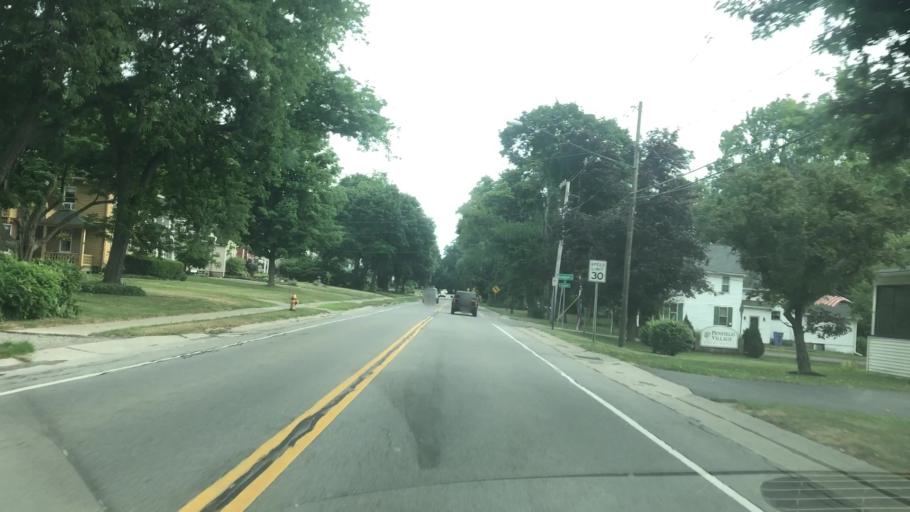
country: US
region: New York
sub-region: Monroe County
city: East Rochester
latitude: 43.1269
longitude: -77.4759
